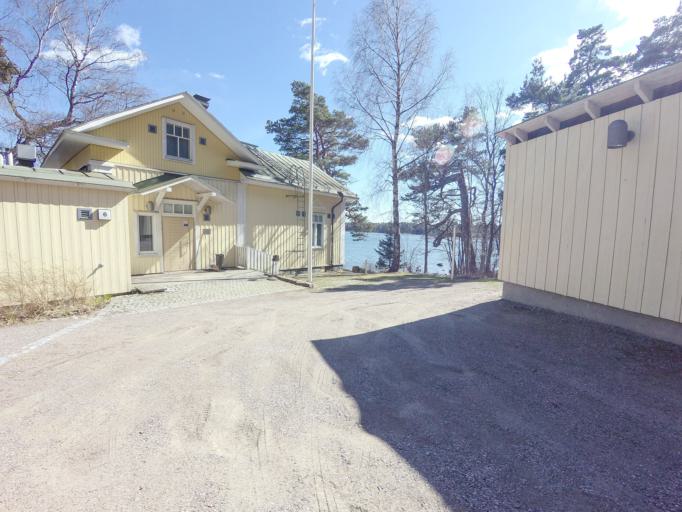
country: FI
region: Uusimaa
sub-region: Helsinki
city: Helsinki
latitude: 60.1581
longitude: 25.0680
